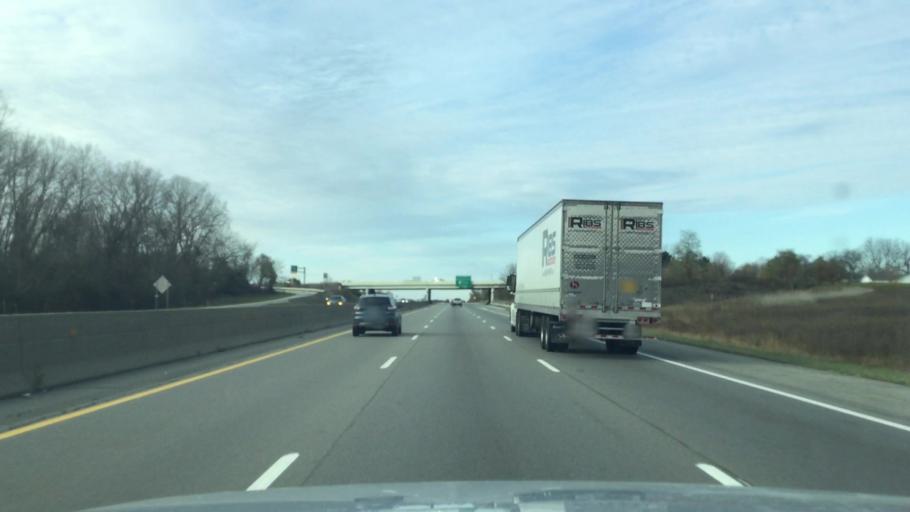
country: US
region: Michigan
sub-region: Washtenaw County
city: Ypsilanti
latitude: 42.2298
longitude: -83.6134
